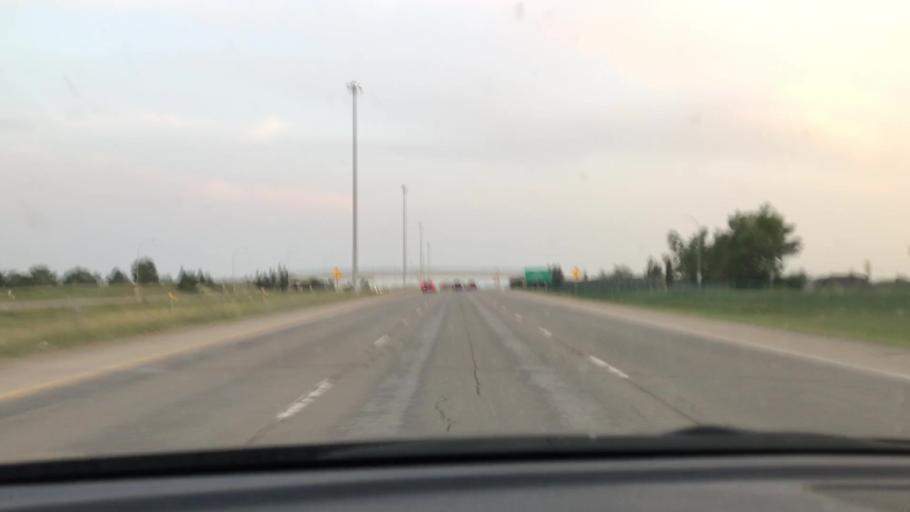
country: CA
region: Alberta
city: Airdrie
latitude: 51.2864
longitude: -114.0012
